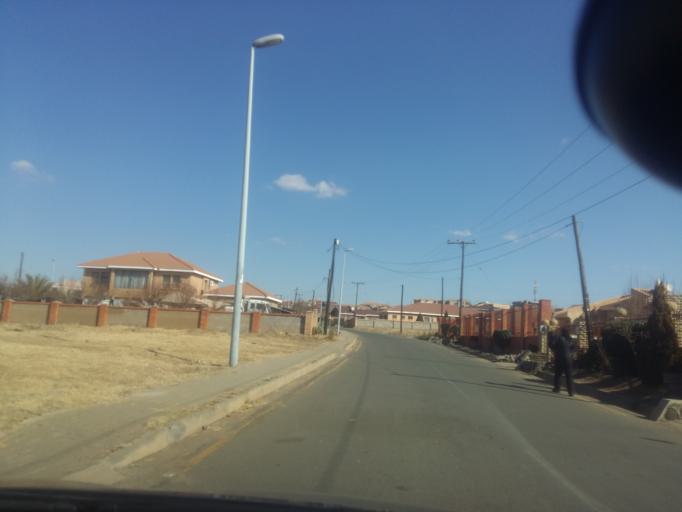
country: LS
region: Maseru
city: Maseru
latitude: -29.3437
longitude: 27.4516
